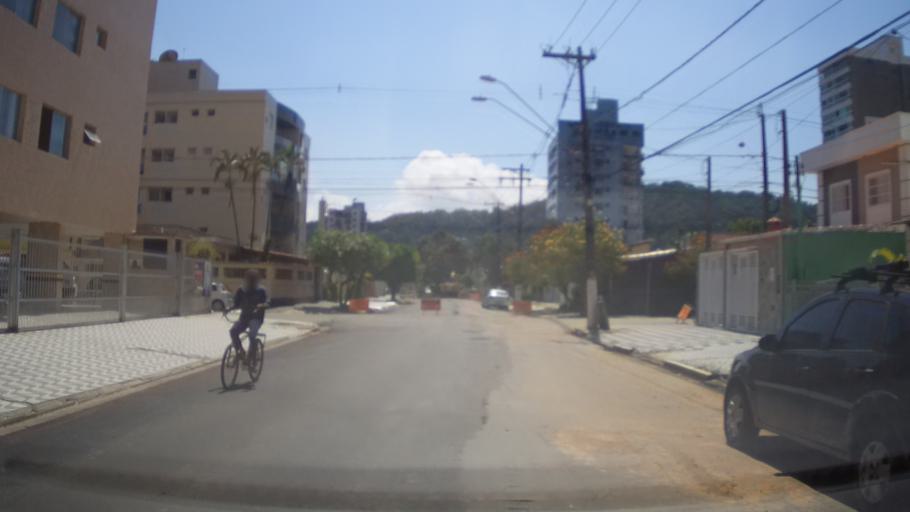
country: BR
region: Sao Paulo
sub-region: Praia Grande
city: Praia Grande
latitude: -24.0069
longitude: -46.4100
